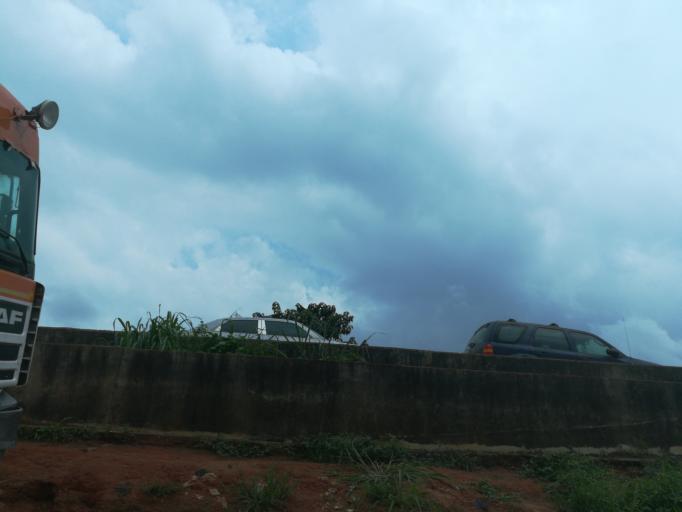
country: NG
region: Lagos
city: Oshodi
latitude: 6.5596
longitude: 3.3239
